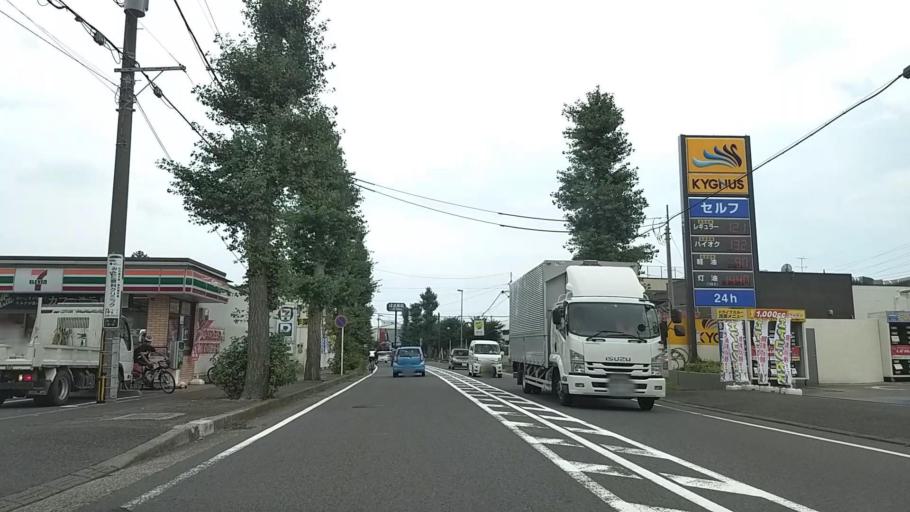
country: JP
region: Kanagawa
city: Minami-rinkan
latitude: 35.4648
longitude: 139.4304
